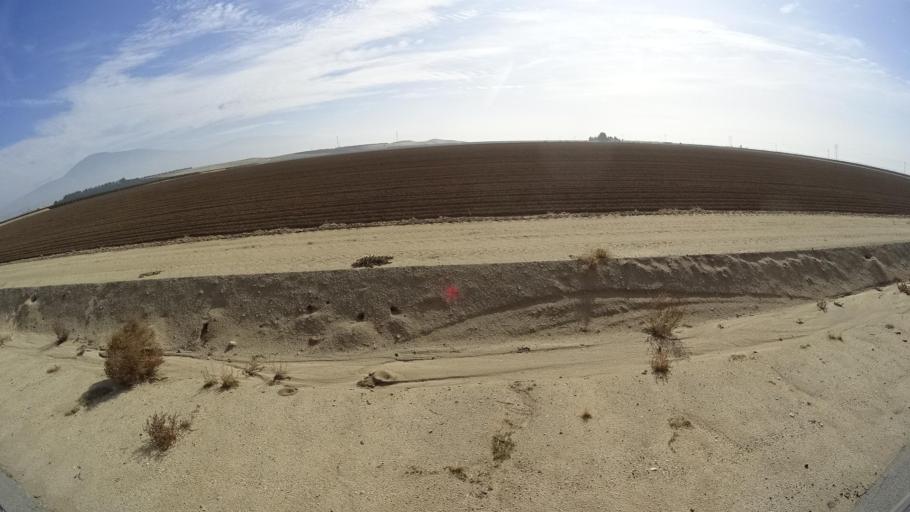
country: US
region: California
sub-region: Kern County
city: Arvin
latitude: 35.3257
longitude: -118.8038
